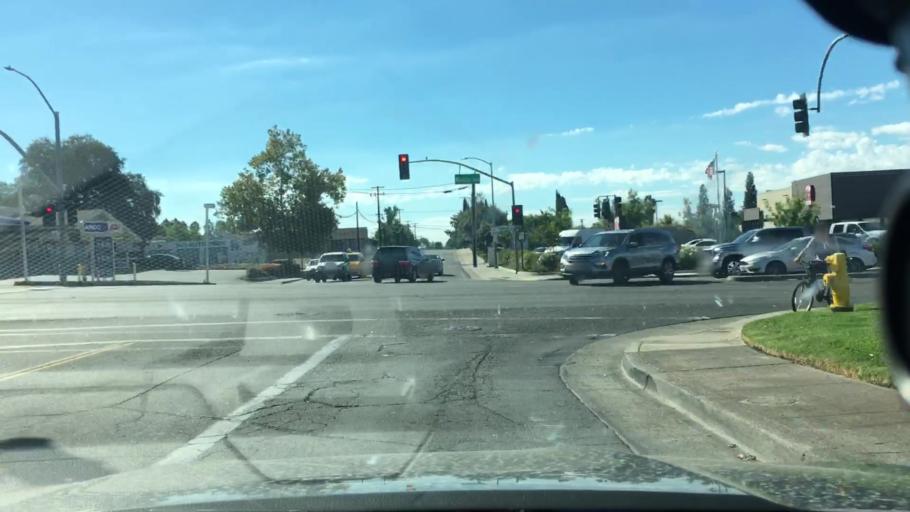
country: US
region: California
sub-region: Sacramento County
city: Foothill Farms
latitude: 38.6613
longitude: -121.3553
